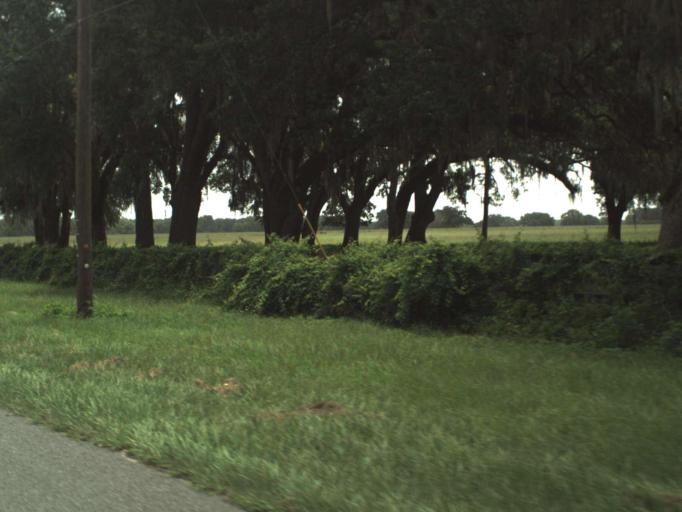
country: US
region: Florida
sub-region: Sumter County
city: Lake Panasoffkee
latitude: 28.7125
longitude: -82.0985
